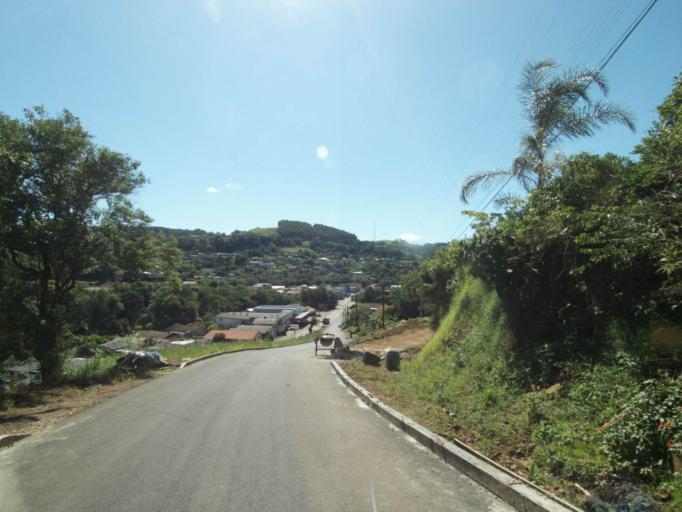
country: BR
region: Parana
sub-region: Ampere
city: Ampere
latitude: -26.1739
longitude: -53.3573
